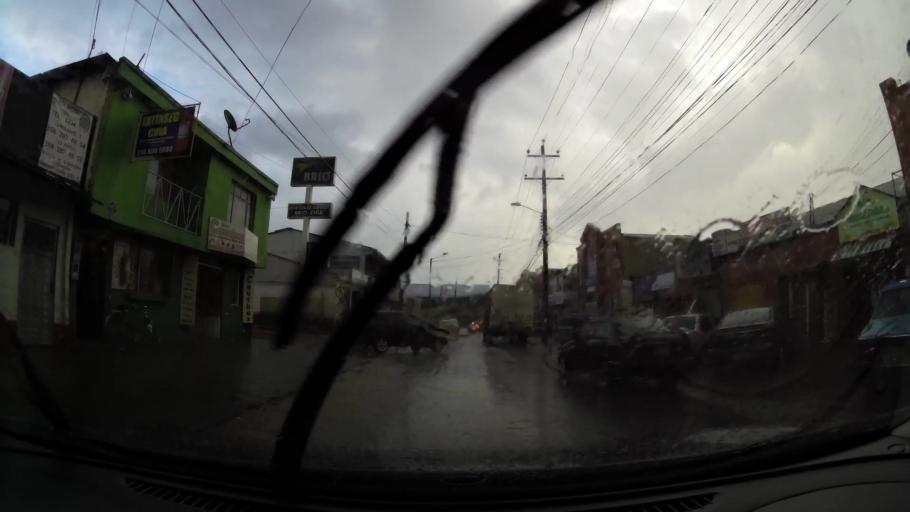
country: CO
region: Cundinamarca
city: Chia
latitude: 4.8603
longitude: -74.0628
